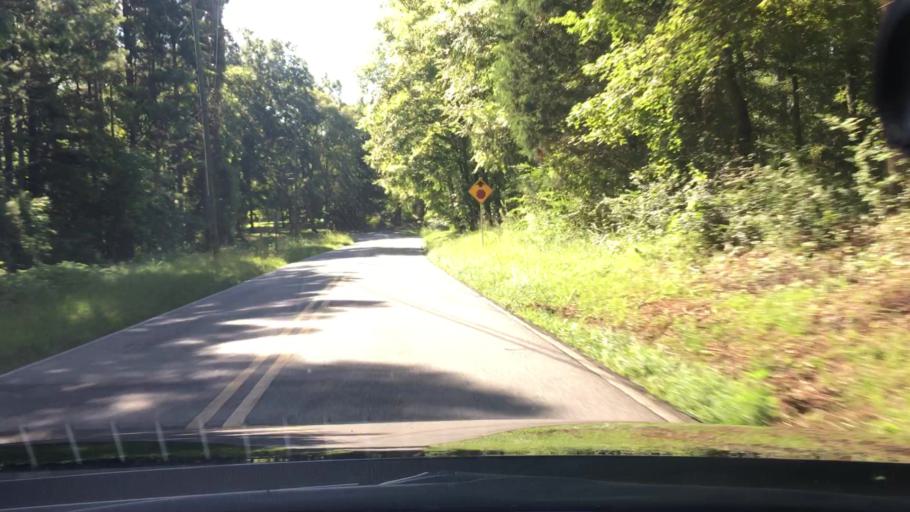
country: US
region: Georgia
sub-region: Putnam County
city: Jefferson
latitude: 33.4322
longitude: -83.3723
